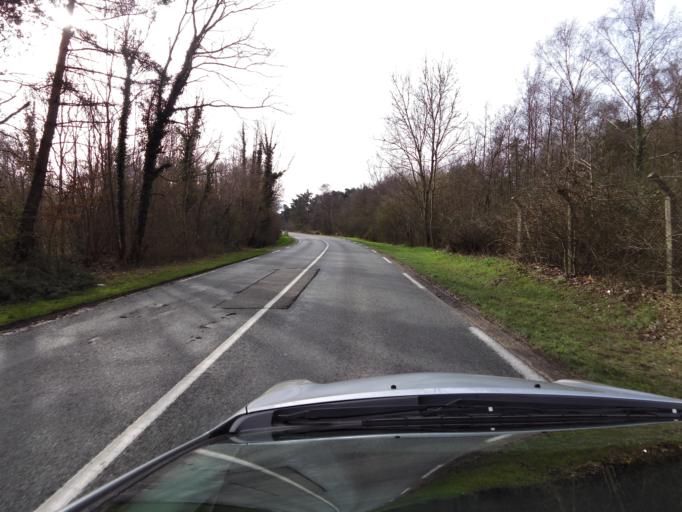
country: FR
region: Picardie
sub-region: Departement de l'Oise
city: Ver-sur-Launette
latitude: 49.1422
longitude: 2.6834
